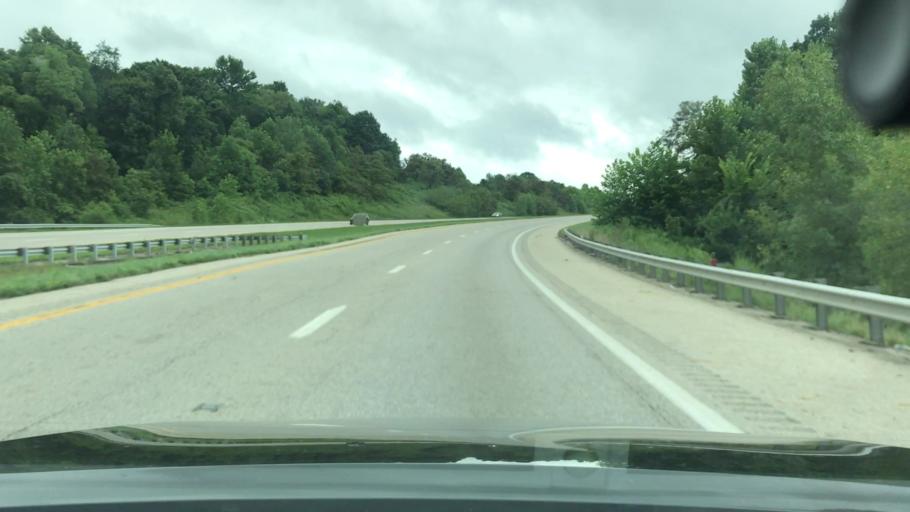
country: US
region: Ohio
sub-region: Ross County
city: Chillicothe
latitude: 39.2551
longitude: -82.8539
